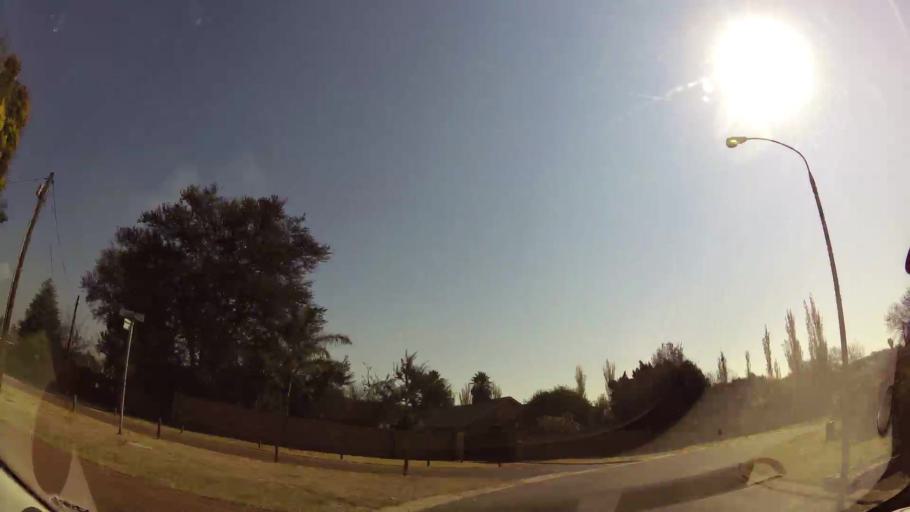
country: ZA
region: Gauteng
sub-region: Ekurhuleni Metropolitan Municipality
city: Boksburg
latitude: -26.1720
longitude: 28.2652
